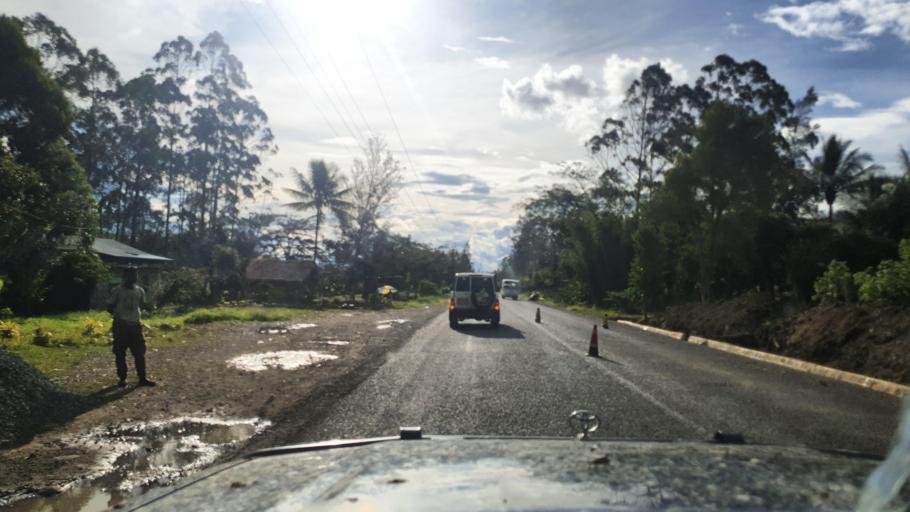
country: PG
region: Jiwaka
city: Minj
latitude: -5.8924
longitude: 144.7383
